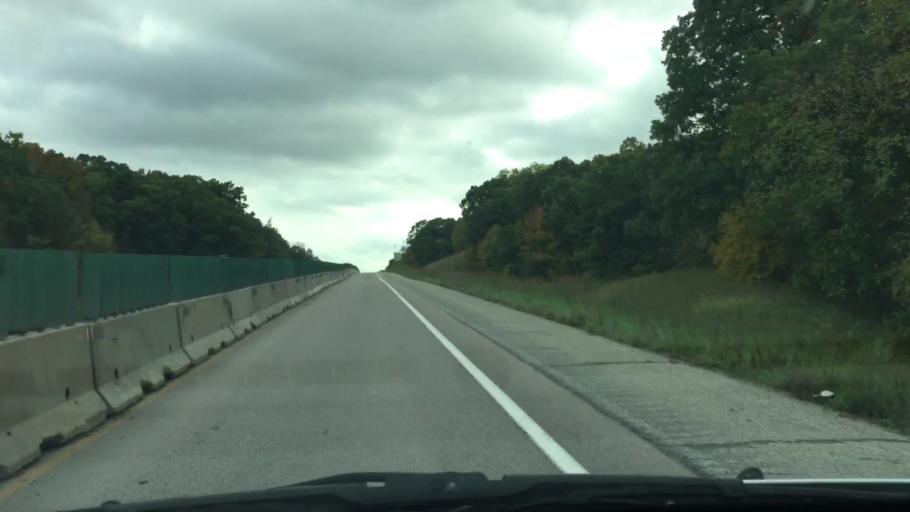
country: US
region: Iowa
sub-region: Decatur County
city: Leon
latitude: 40.7069
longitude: -93.8458
